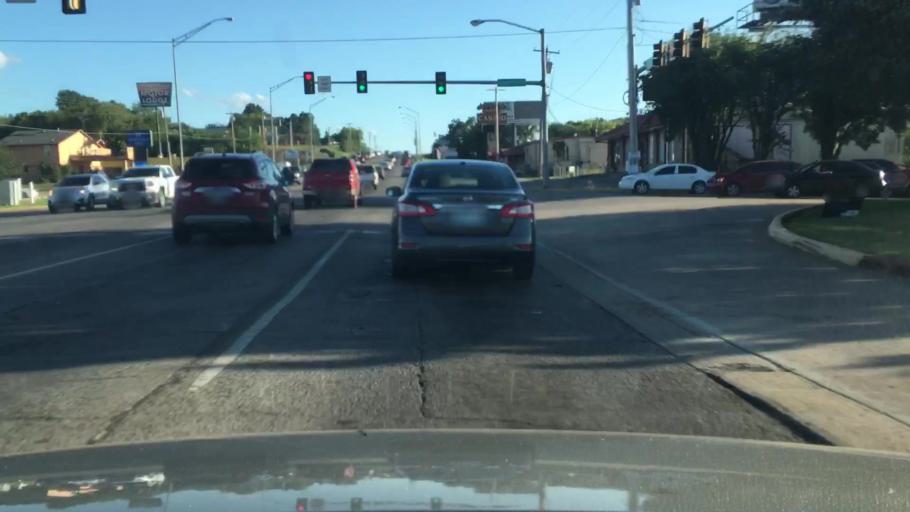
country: US
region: Oklahoma
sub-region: Cherokee County
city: Tahlequah
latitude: 35.8883
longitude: -94.9771
